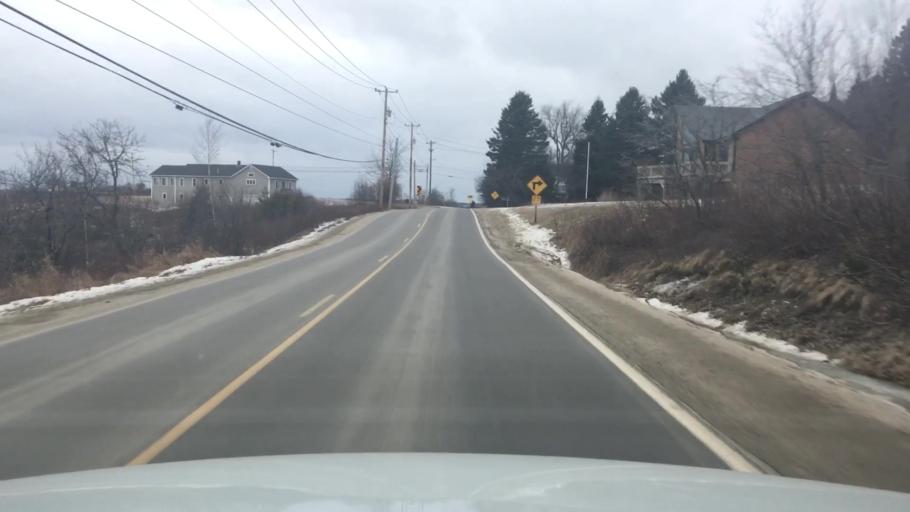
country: US
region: Maine
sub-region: Washington County
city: Addison
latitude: 44.6212
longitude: -67.7093
